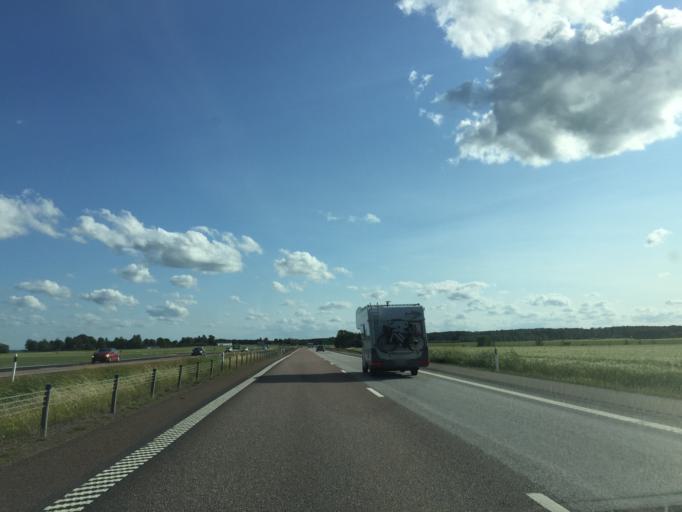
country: SE
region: OErebro
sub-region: Kumla Kommun
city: Kumla
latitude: 59.1624
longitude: 15.1078
